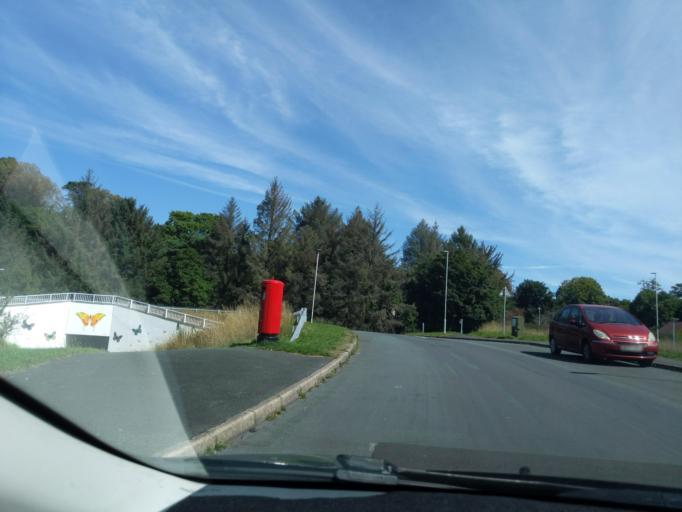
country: GB
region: England
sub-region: Devon
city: Plympton
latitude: 50.3859
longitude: -4.0301
